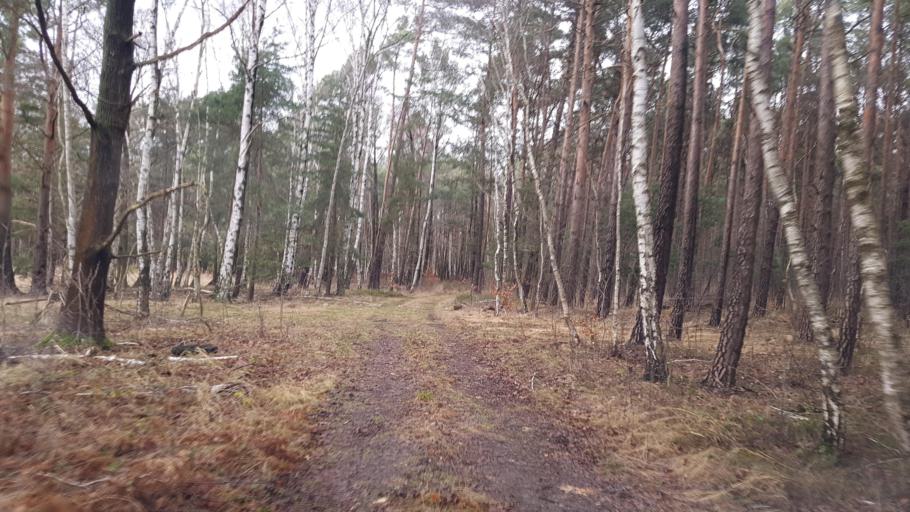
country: DE
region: Brandenburg
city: Ruckersdorf
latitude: 51.5580
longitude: 13.6184
